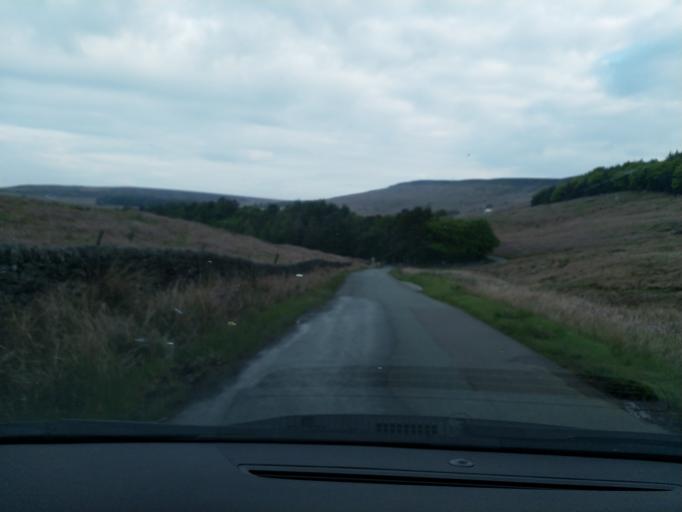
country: GB
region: England
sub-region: Derbyshire
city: Hathersage
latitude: 53.3471
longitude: -1.6394
